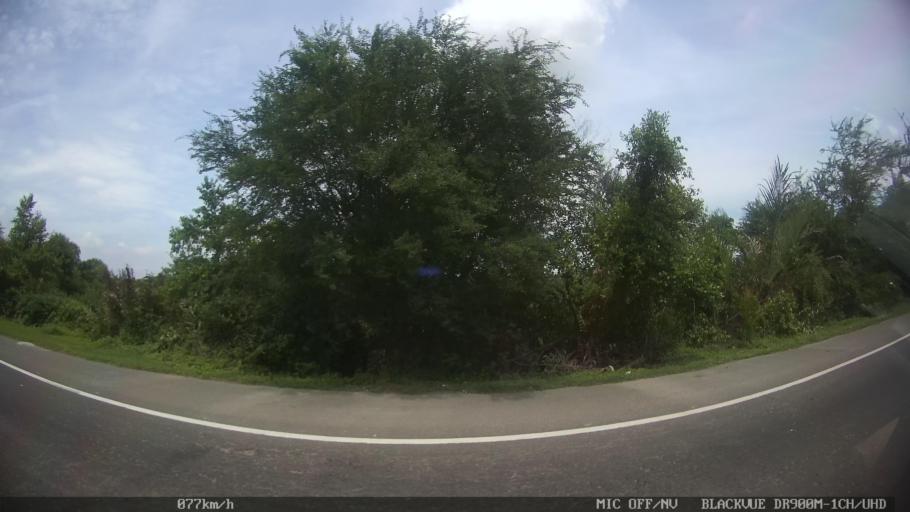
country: ID
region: North Sumatra
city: Belawan
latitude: 3.7672
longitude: 98.6840
